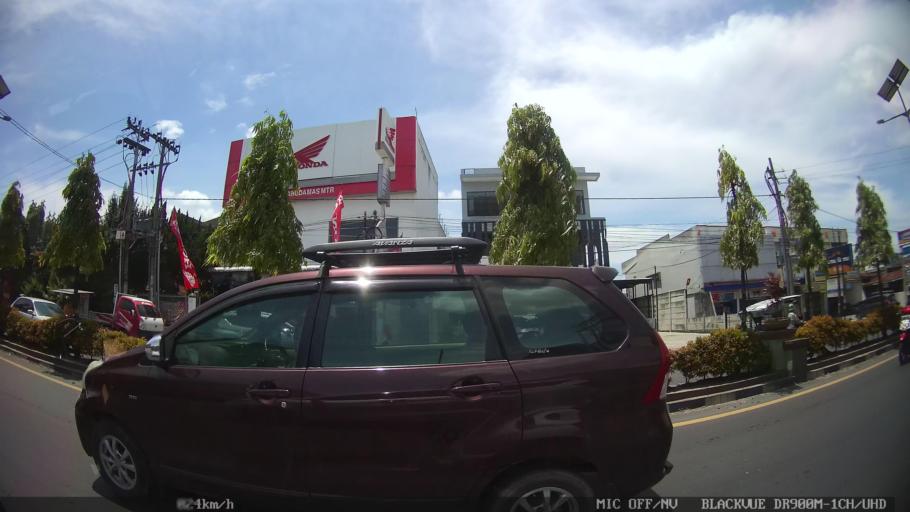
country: ID
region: North Sumatra
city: Binjai
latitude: 3.6086
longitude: 98.5009
